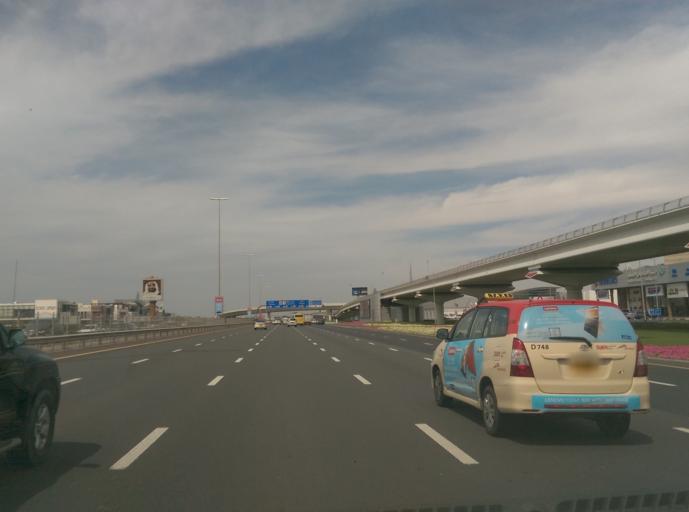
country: AE
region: Dubai
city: Dubai
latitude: 25.1355
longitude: 55.2154
